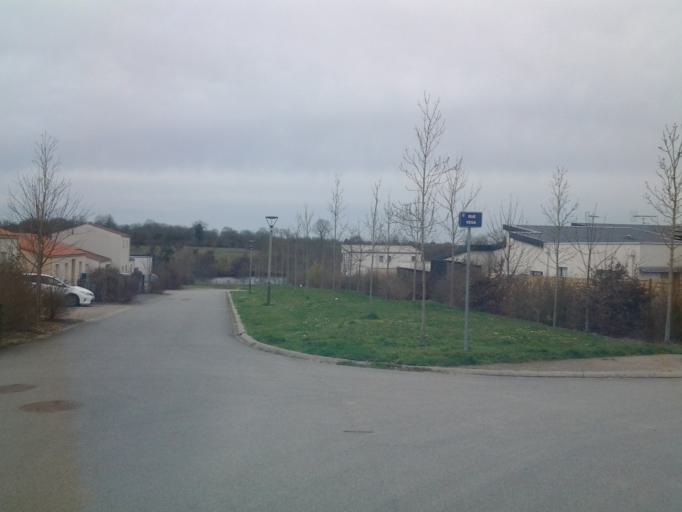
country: FR
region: Pays de la Loire
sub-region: Departement de la Vendee
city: La Roche-sur-Yon
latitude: 46.6546
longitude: -1.3960
